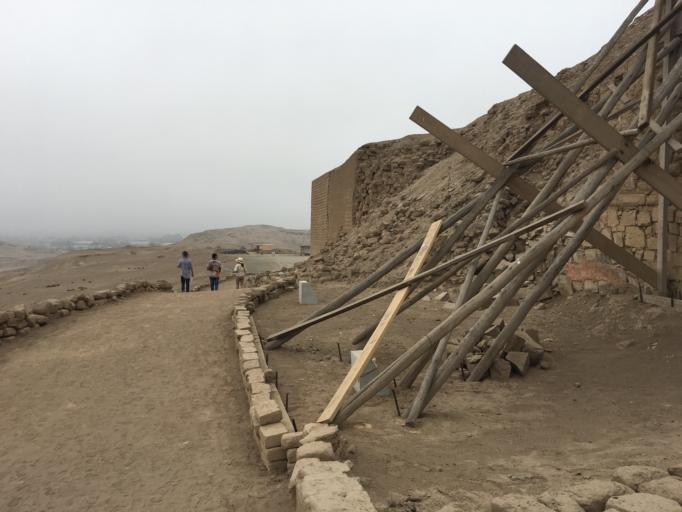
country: PE
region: Lima
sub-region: Lima
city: Punta Hermosa
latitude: -12.2620
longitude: -76.9019
